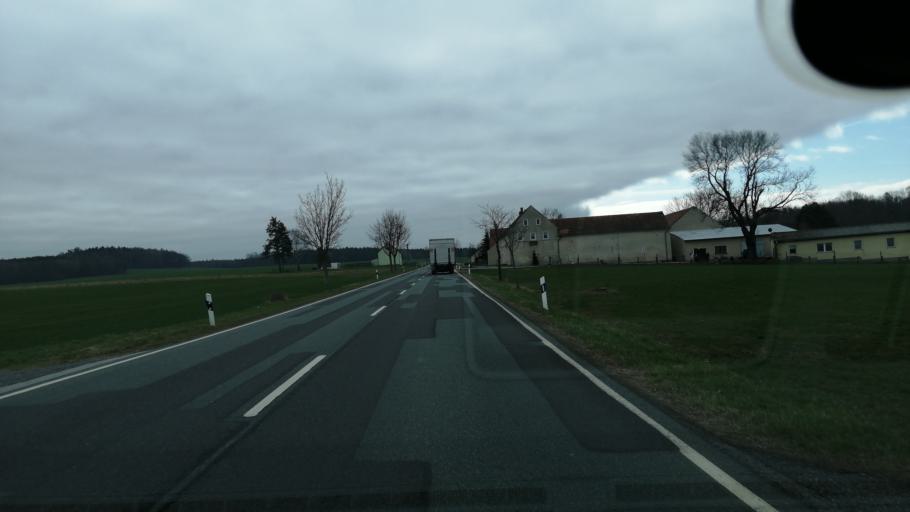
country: DE
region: Saxony
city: Niedercunnersdorf
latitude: 51.0598
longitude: 14.6946
